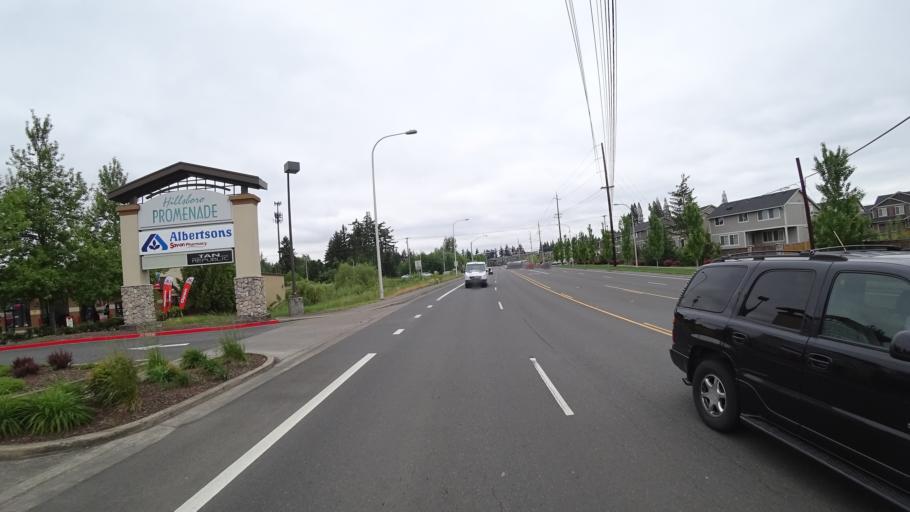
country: US
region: Oregon
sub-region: Washington County
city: Aloha
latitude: 45.5143
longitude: -122.9018
